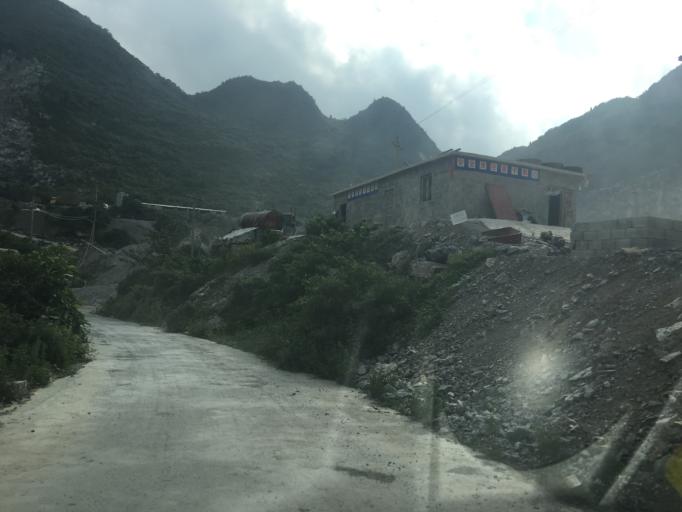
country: CN
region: Guangxi Zhuangzu Zizhiqu
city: Xinzhou
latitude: 25.0673
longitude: 105.7234
